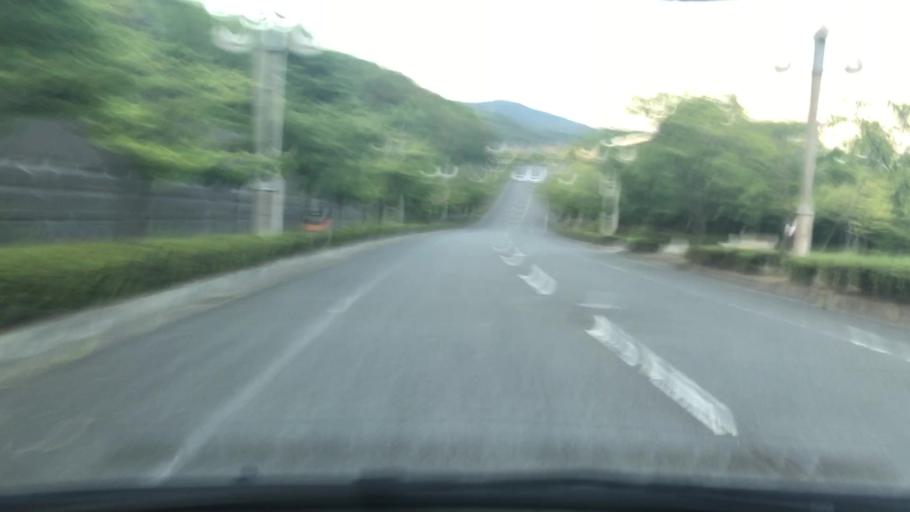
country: JP
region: Hyogo
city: Takarazuka
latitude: 34.8345
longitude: 135.3037
